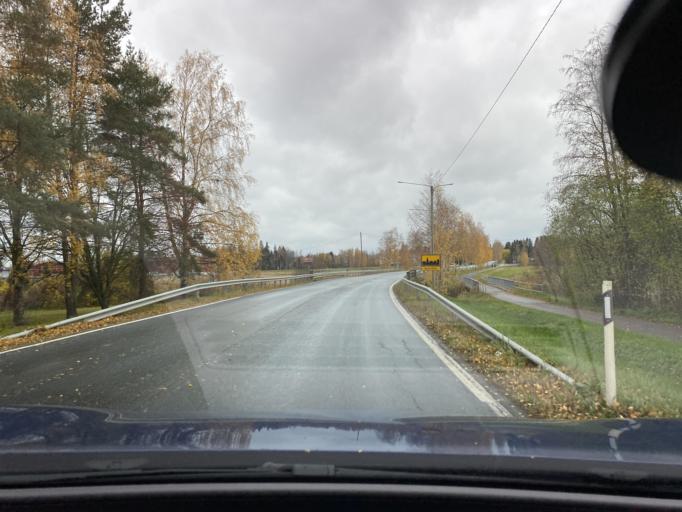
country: FI
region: Satakunta
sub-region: Pori
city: Kokemaeki
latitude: 61.2559
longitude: 22.3678
